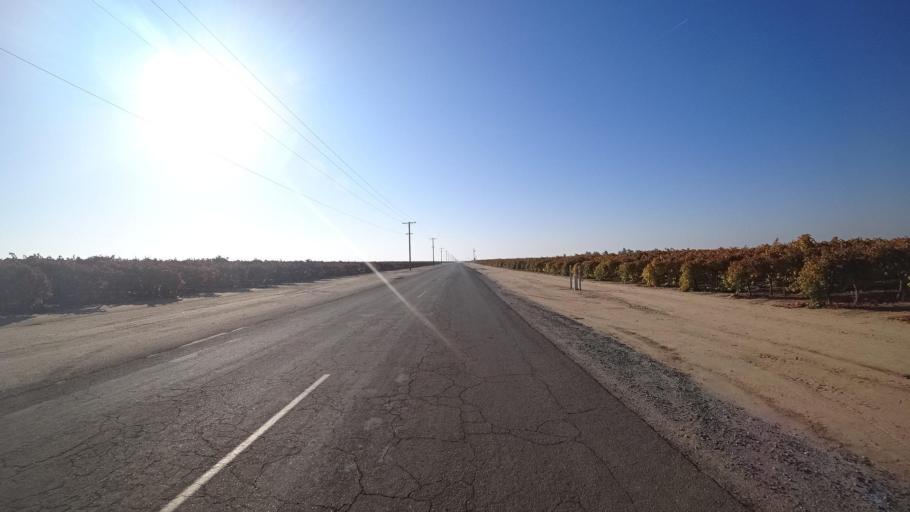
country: US
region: California
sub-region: Tulare County
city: Richgrove
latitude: 35.7570
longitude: -119.1696
